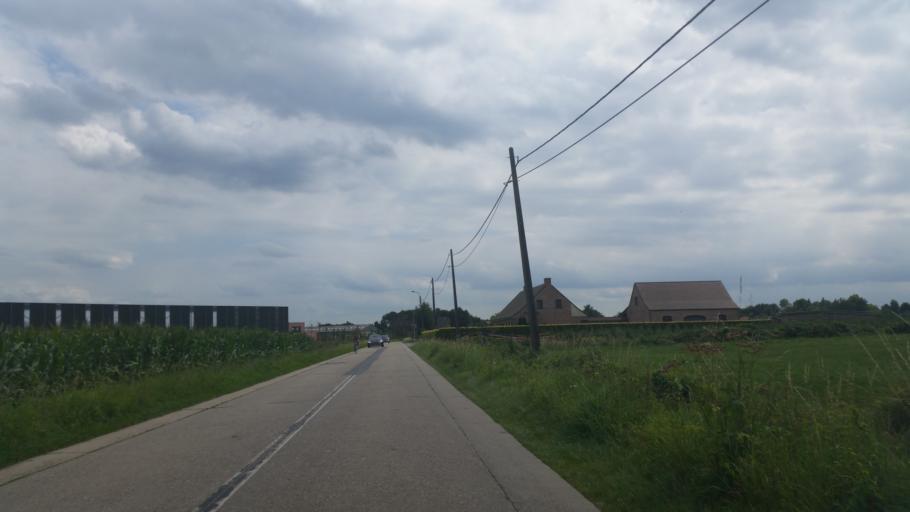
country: BE
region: Flanders
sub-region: Provincie Antwerpen
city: Hoogstraten
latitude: 51.4055
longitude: 4.7965
